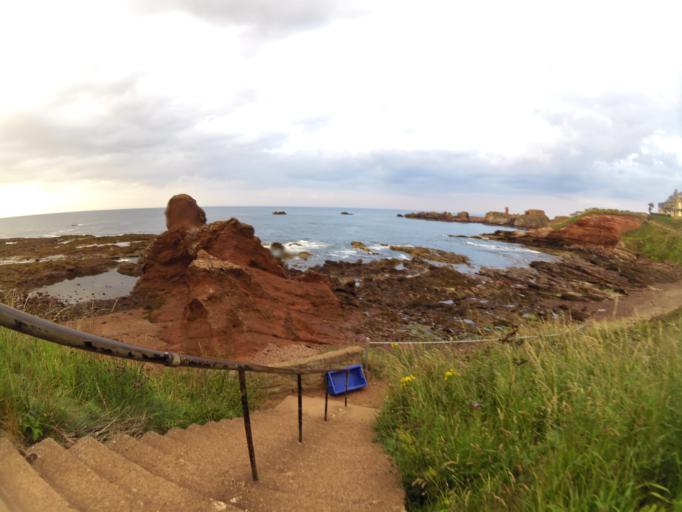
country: GB
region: Scotland
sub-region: East Lothian
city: Dunbar
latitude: 56.0053
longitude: -2.5248
